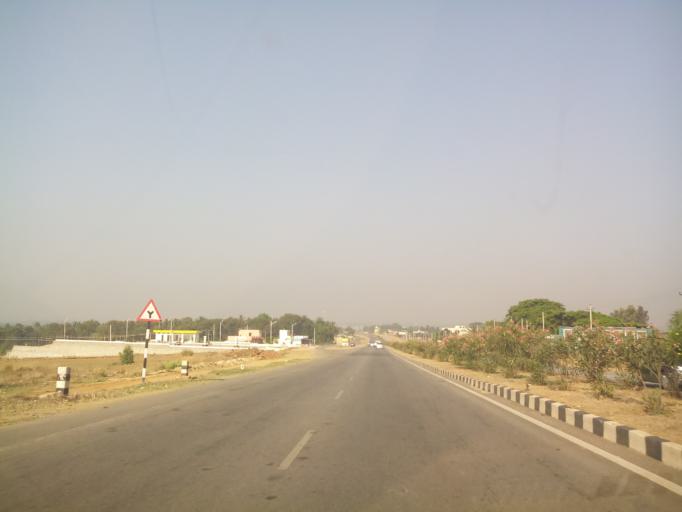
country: IN
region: Karnataka
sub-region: Bangalore Rural
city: Nelamangala
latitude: 13.0659
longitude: 77.3561
